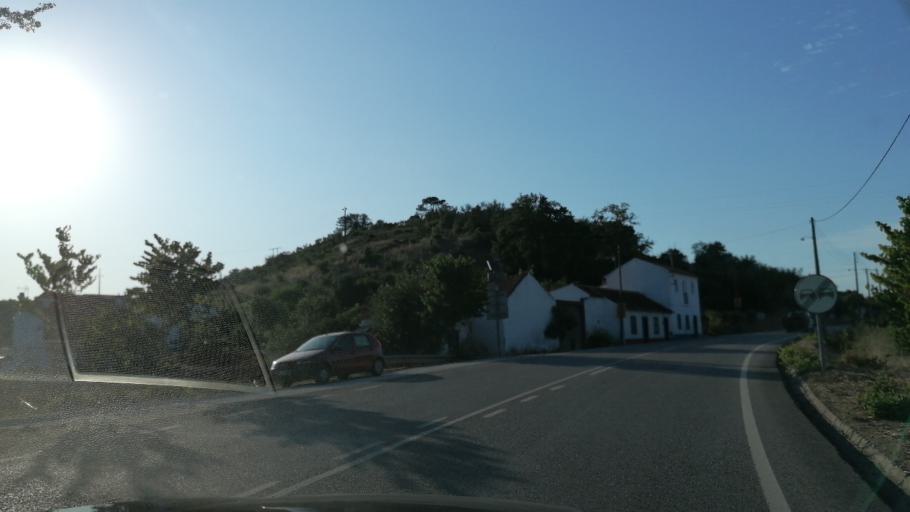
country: PT
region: Santarem
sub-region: Alcanena
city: Alcanena
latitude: 39.3662
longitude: -8.6565
